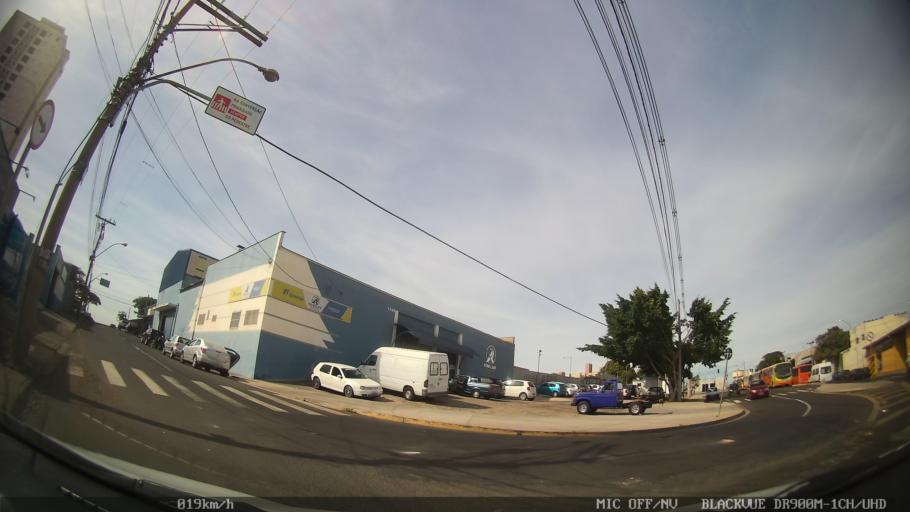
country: BR
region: Sao Paulo
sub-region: Piracicaba
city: Piracicaba
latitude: -22.7500
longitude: -47.6492
